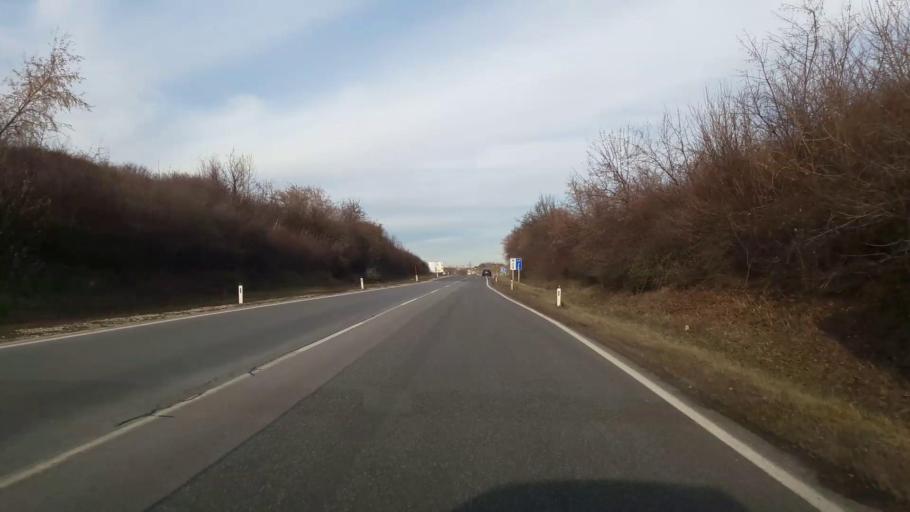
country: AT
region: Lower Austria
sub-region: Politischer Bezirk Mistelbach
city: Gaweinstal
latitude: 48.4910
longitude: 16.5966
